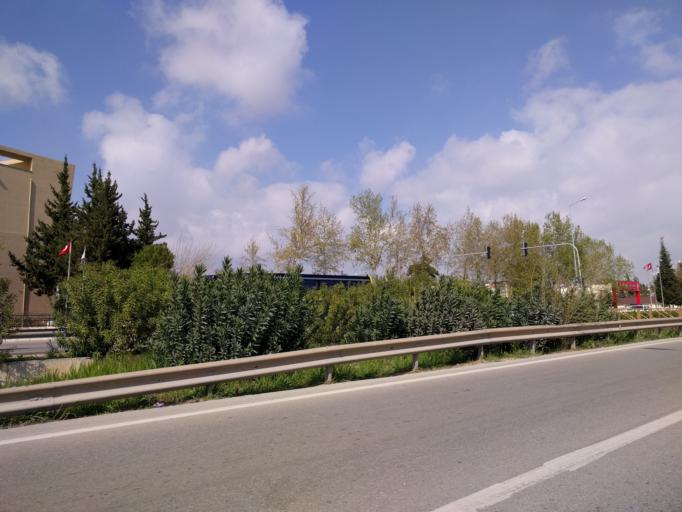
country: TR
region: Antalya
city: Antalya
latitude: 36.9008
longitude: 30.6423
